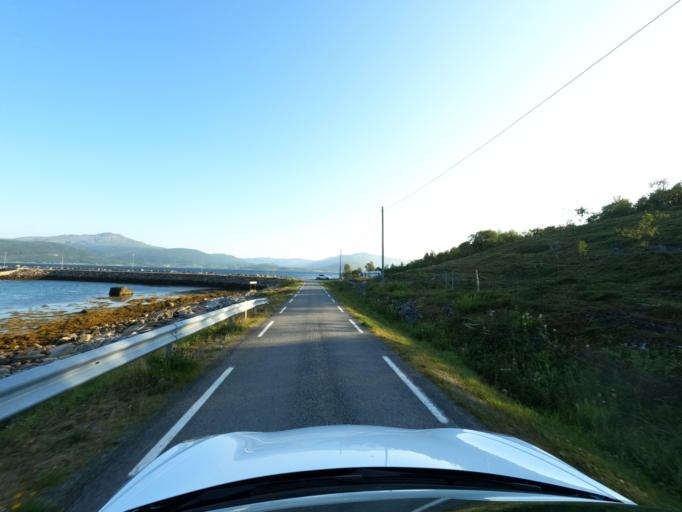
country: NO
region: Troms
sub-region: Skanland
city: Evenskjer
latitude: 68.4569
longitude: 16.6923
